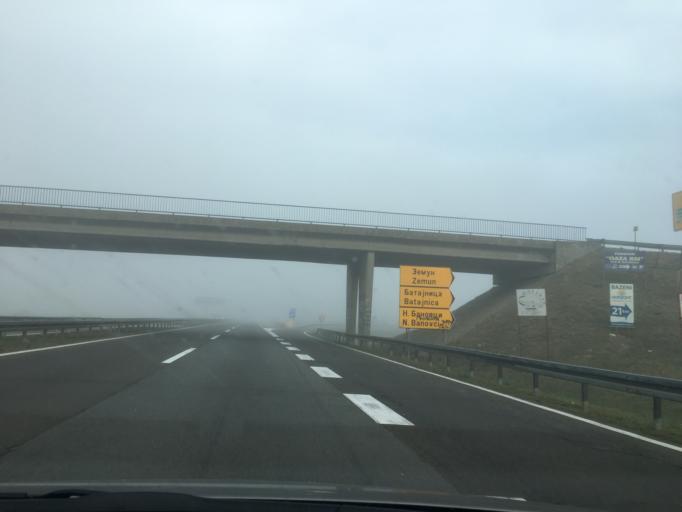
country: RS
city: Novi Banovci
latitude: 44.9433
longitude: 20.2821
